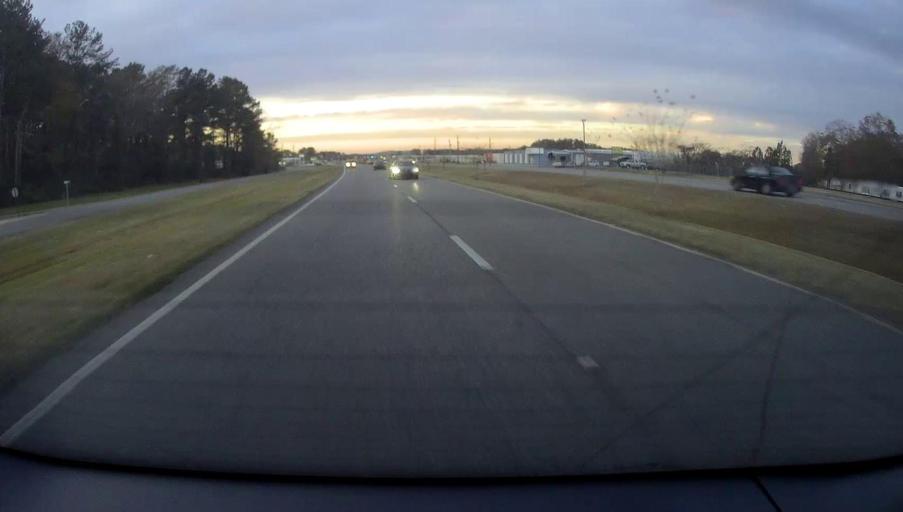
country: US
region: Alabama
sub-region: Etowah County
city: Glencoe
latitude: 33.9614
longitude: -85.9372
